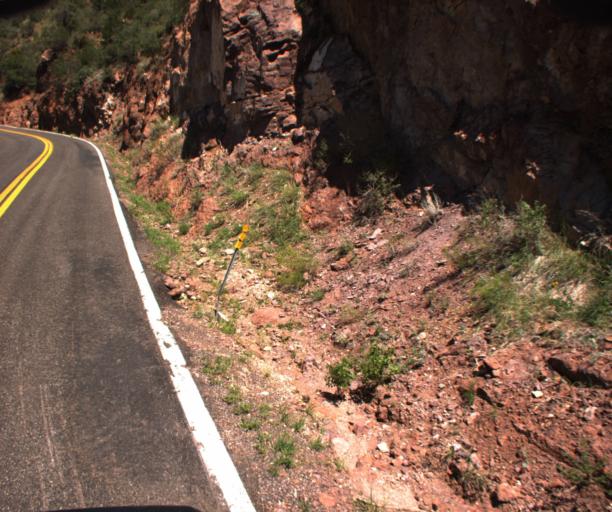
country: US
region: Arizona
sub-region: Greenlee County
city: Morenci
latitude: 33.1664
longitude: -109.3669
